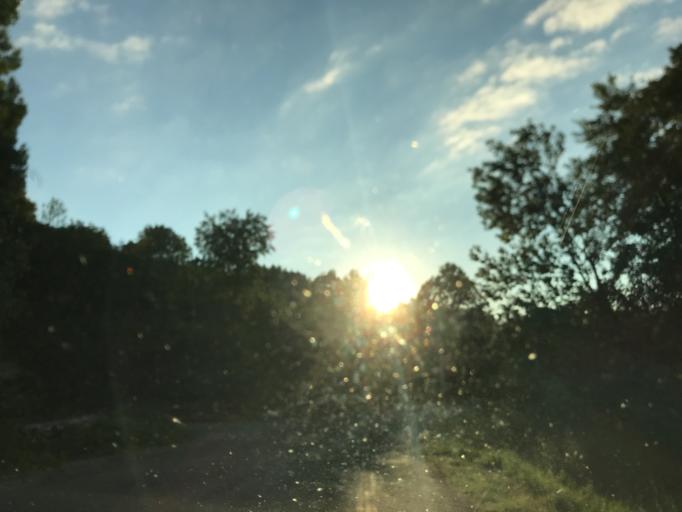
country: FR
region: Rhone-Alpes
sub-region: Departement de la Loire
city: Noiretable
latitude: 45.7947
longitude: 3.7718
